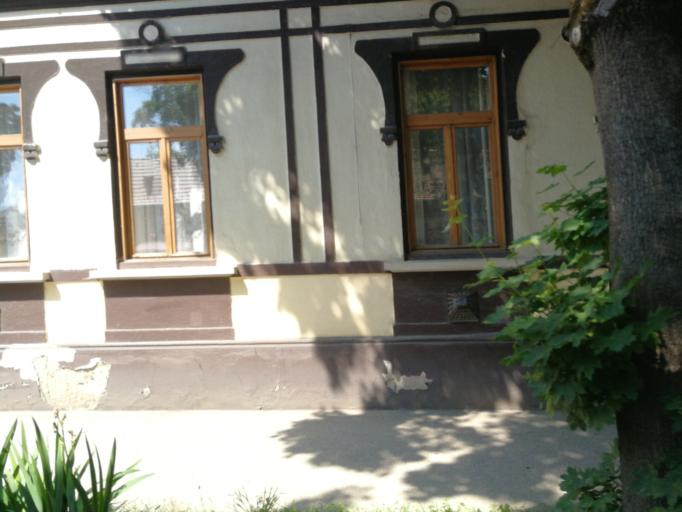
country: HU
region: Vas
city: Sarvar
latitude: 47.2568
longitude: 16.9308
